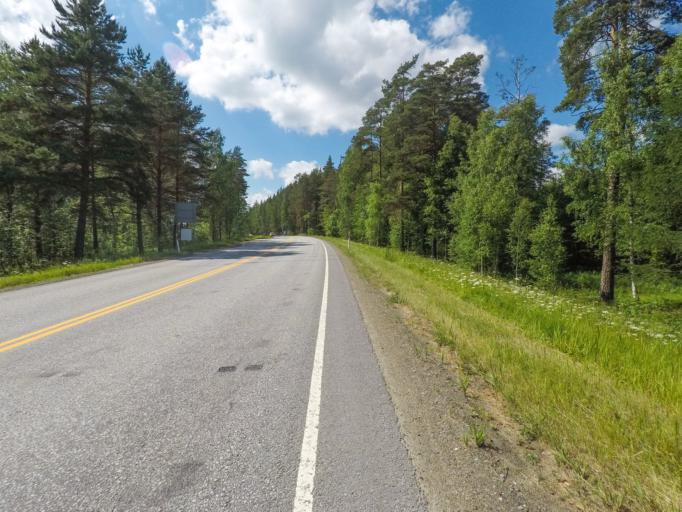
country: FI
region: Southern Savonia
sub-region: Savonlinna
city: Punkaharju
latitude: 61.8048
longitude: 29.3117
